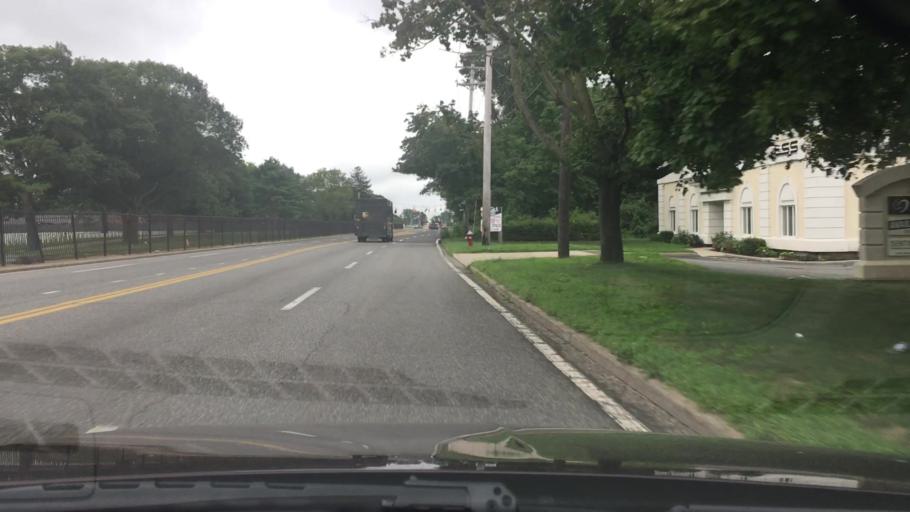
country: US
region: New York
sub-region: Suffolk County
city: East Farmingdale
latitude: 40.7529
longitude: -73.4021
